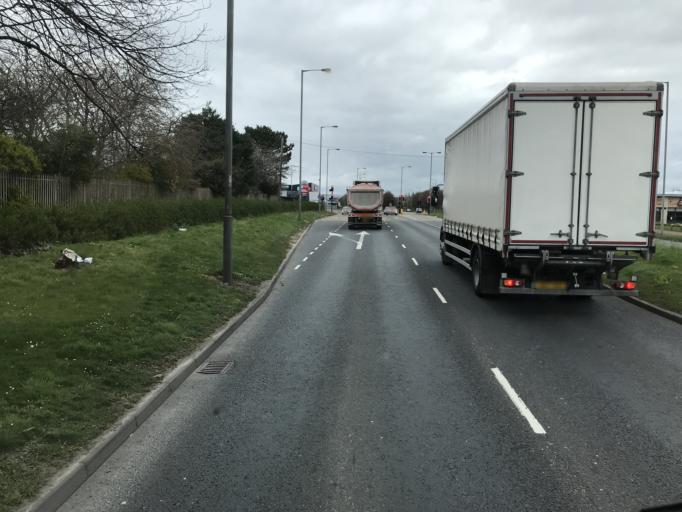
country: GB
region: England
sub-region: Borough of Halton
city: Hale
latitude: 53.3496
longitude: -2.8620
